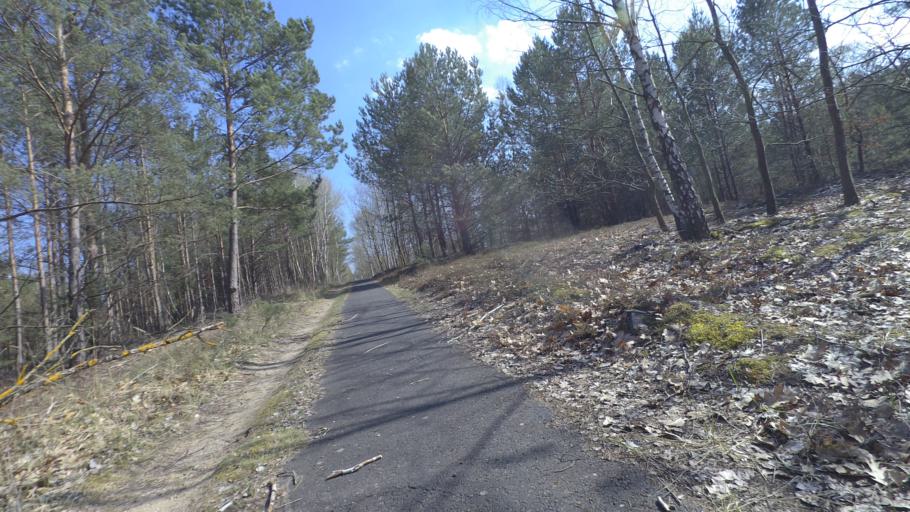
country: DE
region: Brandenburg
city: Mittenwalde
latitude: 52.1830
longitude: 13.5497
